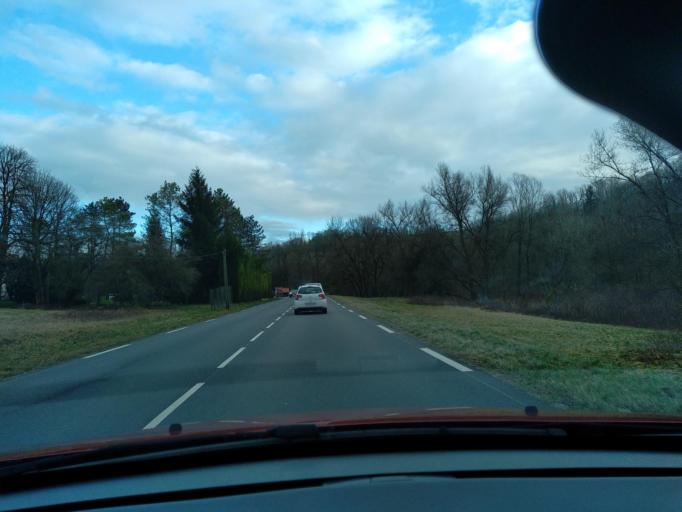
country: FR
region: Rhone-Alpes
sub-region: Departement de la Haute-Savoie
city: Frangy
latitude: 46.0245
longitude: 5.9021
